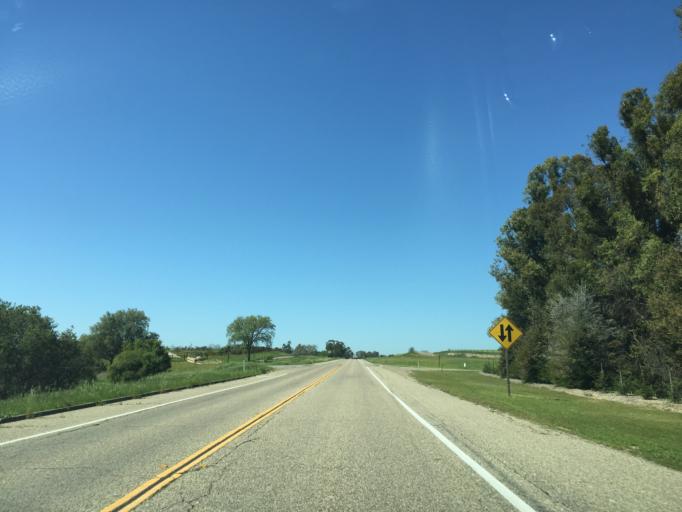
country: US
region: California
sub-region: Santa Barbara County
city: Santa Ynez
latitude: 34.6232
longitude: -120.0702
